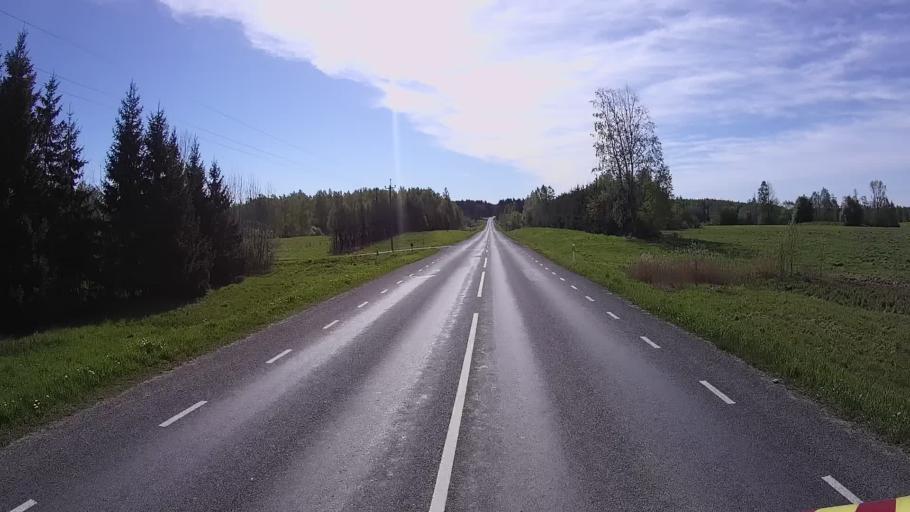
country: EE
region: Polvamaa
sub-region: Polva linn
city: Polva
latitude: 58.1883
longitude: 27.0920
